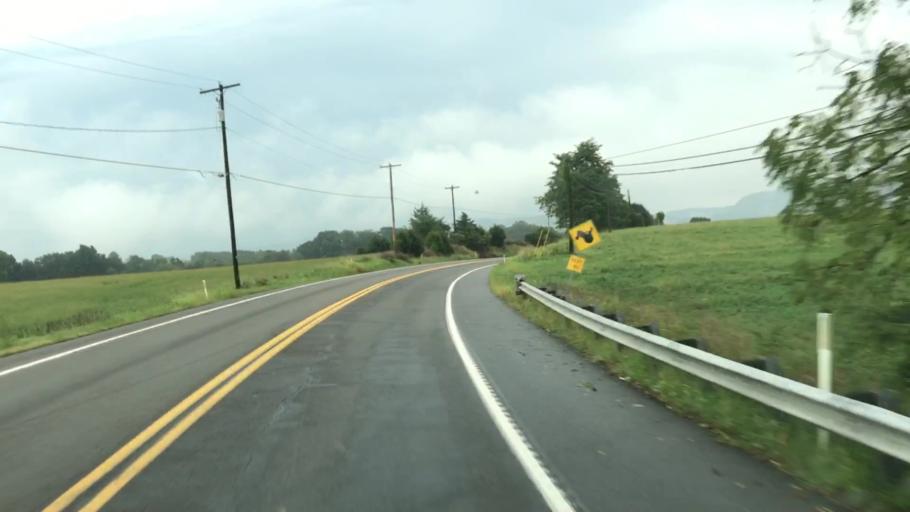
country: US
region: Pennsylvania
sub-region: Perry County
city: Duncannon
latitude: 40.4085
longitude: -77.0941
